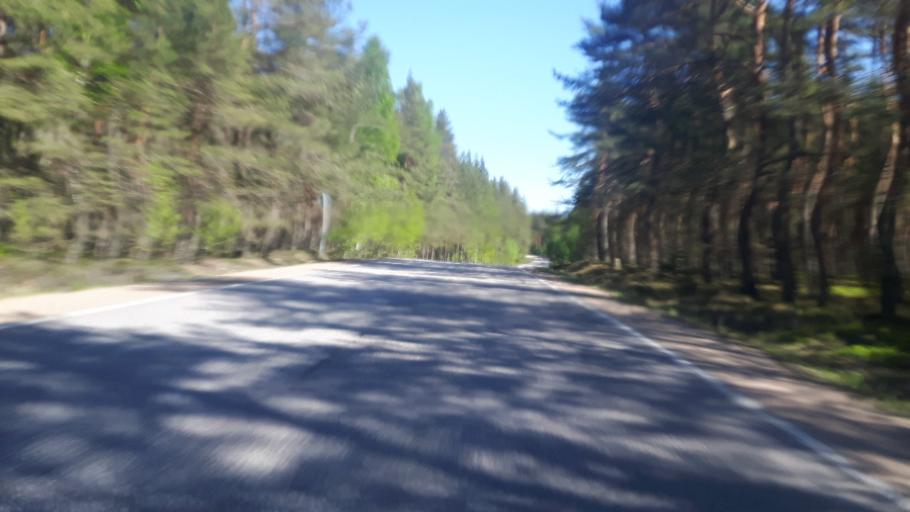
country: RU
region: Leningrad
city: Glebychevo
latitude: 60.2774
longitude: 28.9022
